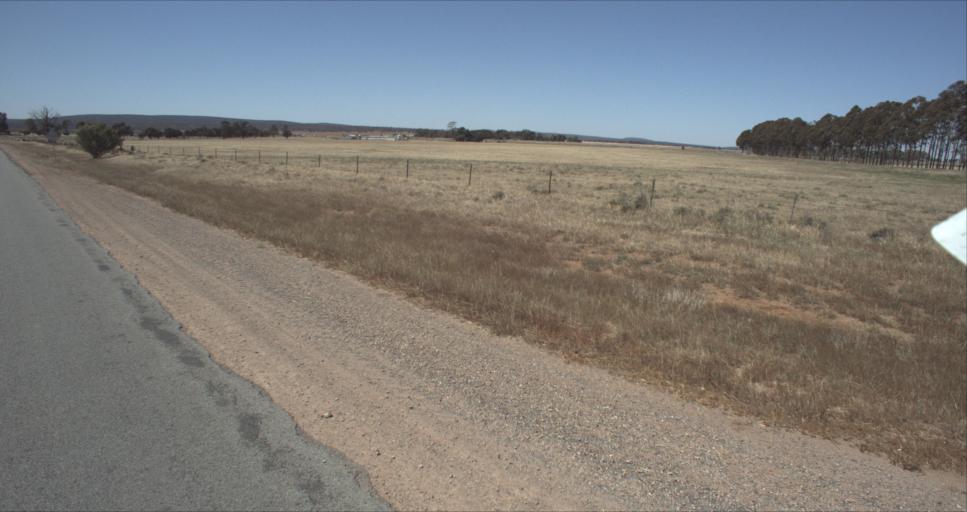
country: AU
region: New South Wales
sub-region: Leeton
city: Leeton
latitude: -34.5355
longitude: 146.4451
